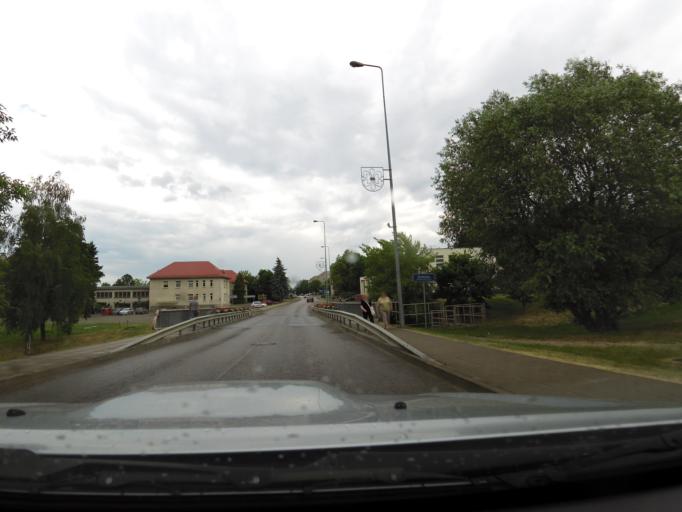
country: LT
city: Vilkaviskis
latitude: 54.6494
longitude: 23.0319
